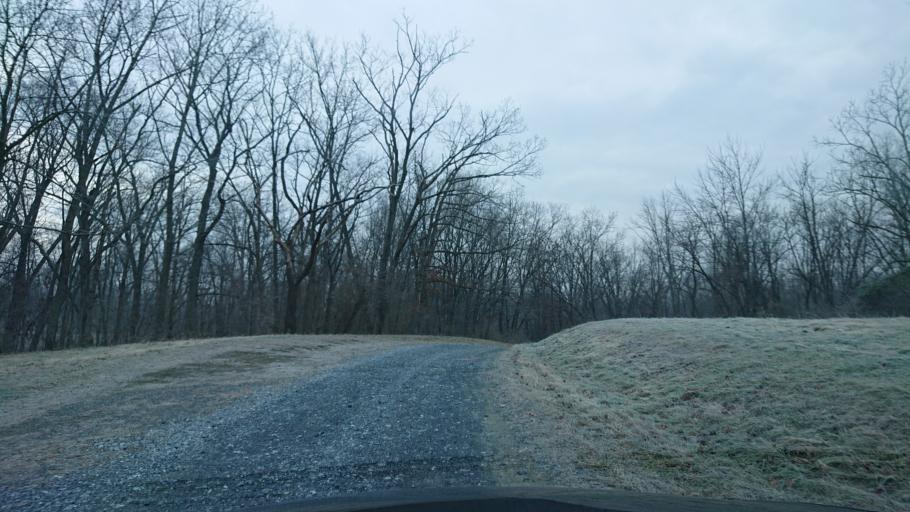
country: US
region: Pennsylvania
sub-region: Lebanon County
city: Palmyra
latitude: 40.4163
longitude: -76.5868
